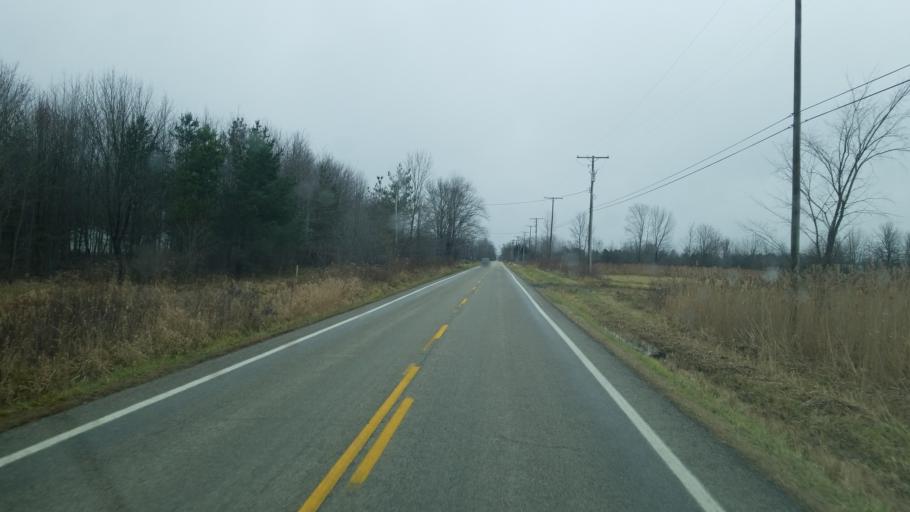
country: US
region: Ohio
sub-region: Ashtabula County
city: Roaming Shores
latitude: 41.6084
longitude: -80.7804
